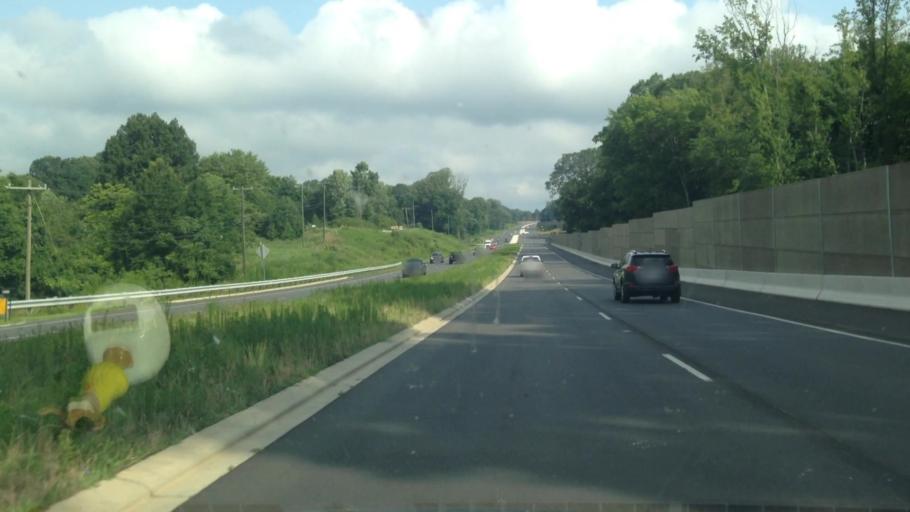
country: US
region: North Carolina
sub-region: Guilford County
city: Summerfield
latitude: 36.1975
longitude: -79.8951
